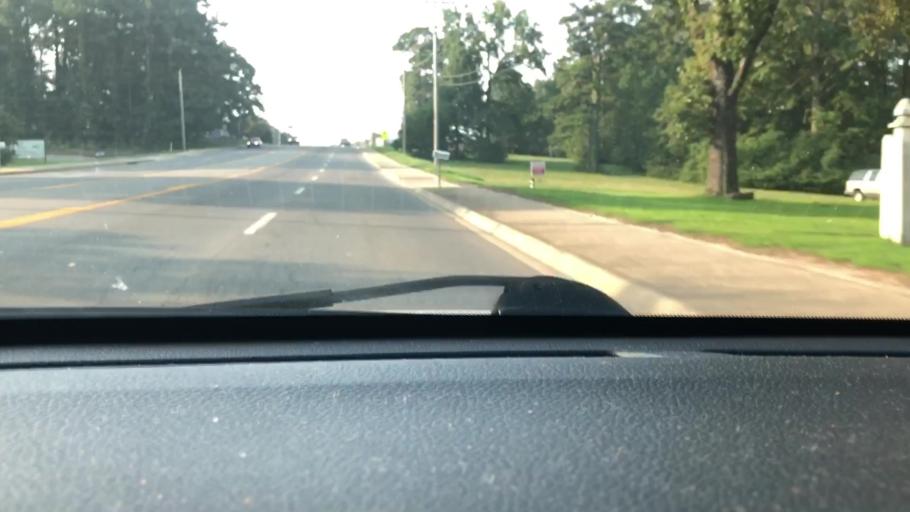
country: US
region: Arkansas
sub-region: Saline County
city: Bryant
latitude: 34.6050
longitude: -92.4914
